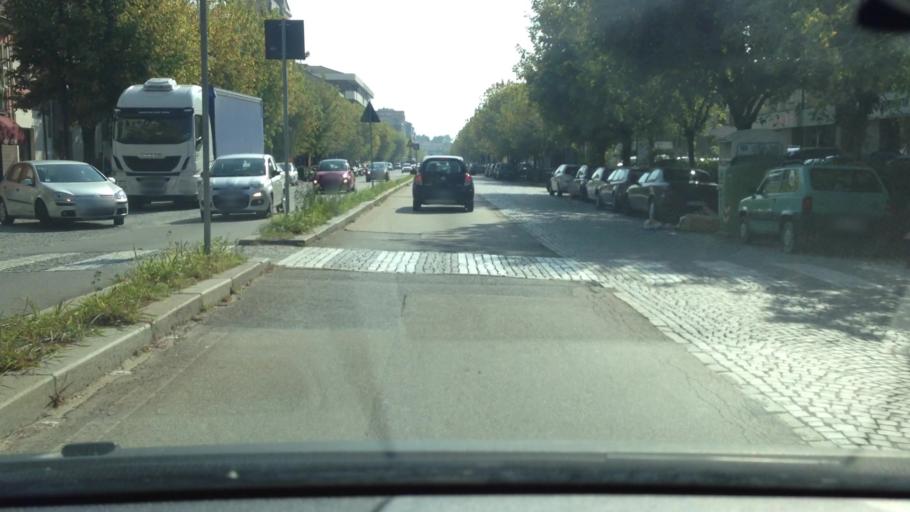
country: IT
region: Piedmont
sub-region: Provincia di Asti
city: Asti
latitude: 44.9046
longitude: 8.1876
